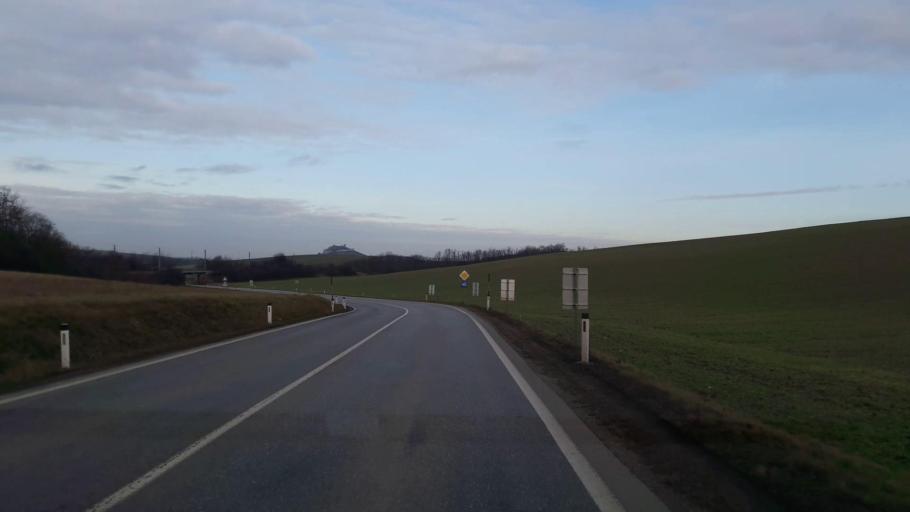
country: AT
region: Lower Austria
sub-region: Politischer Bezirk Mistelbach
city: Staatz
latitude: 48.6483
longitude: 16.5084
